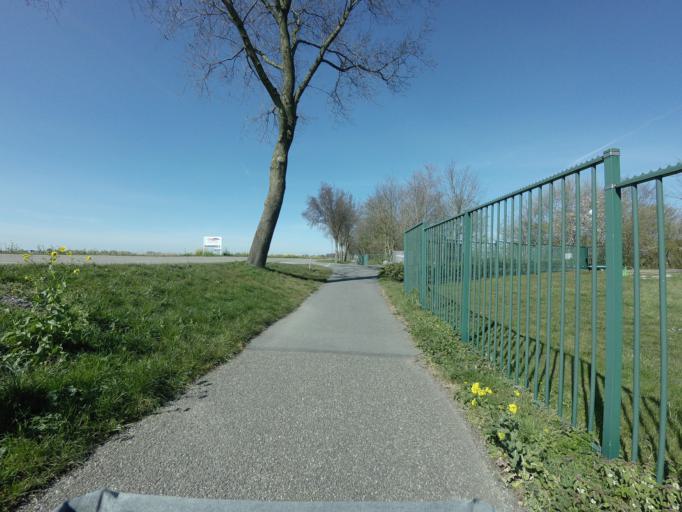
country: NL
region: Utrecht
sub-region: Gemeente De Ronde Venen
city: Mijdrecht
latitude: 52.1785
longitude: 4.8819
